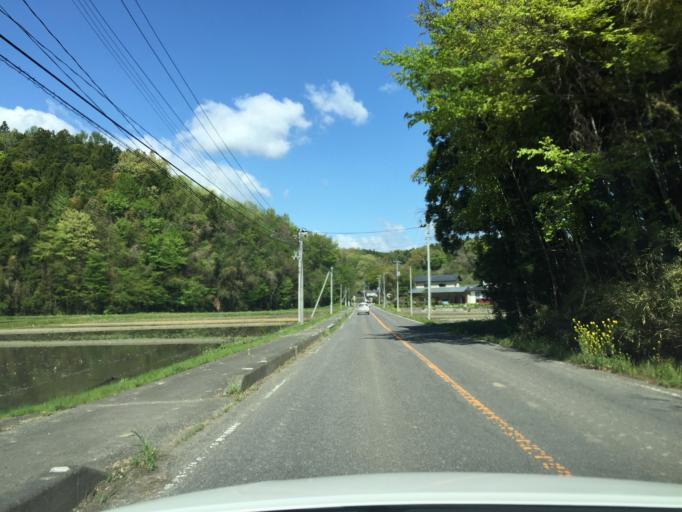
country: JP
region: Fukushima
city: Nihommatsu
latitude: 37.5708
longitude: 140.4873
